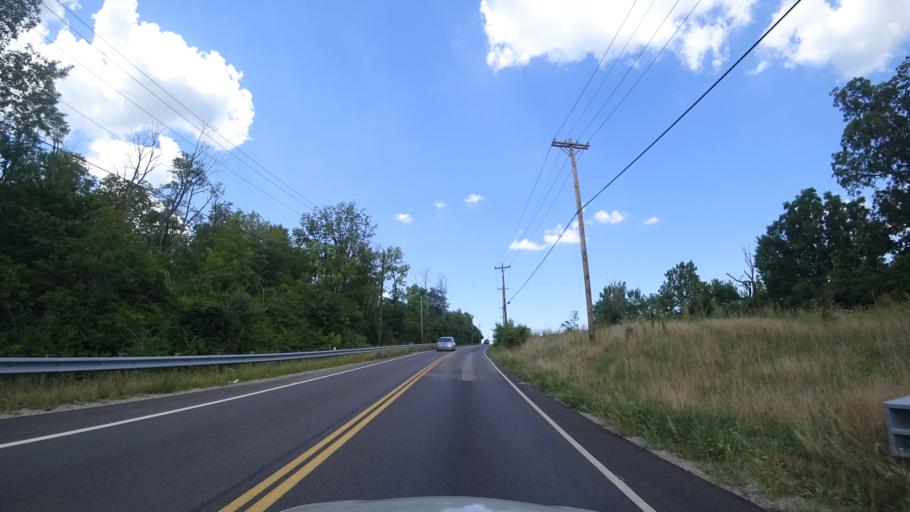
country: US
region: Ohio
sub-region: Butler County
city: Hamilton
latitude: 39.4382
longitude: -84.6080
